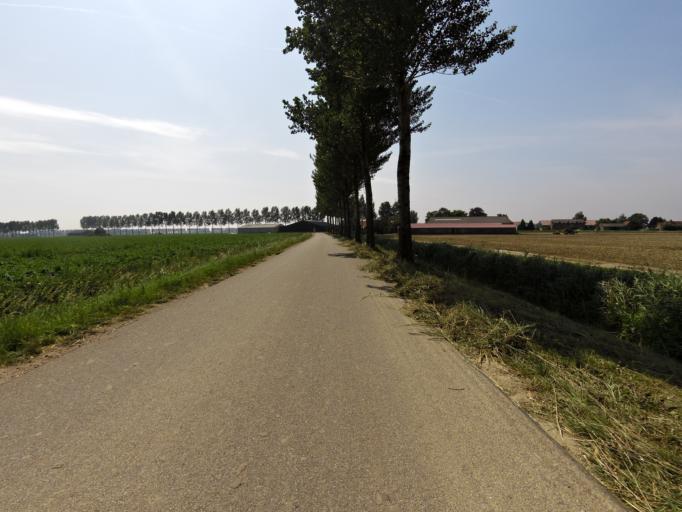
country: NL
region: South Holland
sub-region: Gemeente Dordrecht
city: Dordrecht
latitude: 51.7687
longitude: 4.7170
